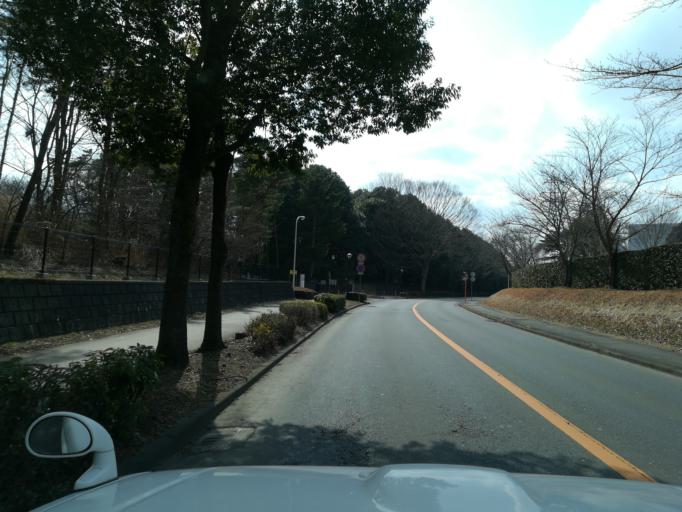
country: JP
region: Ibaraki
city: Naka
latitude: 36.0652
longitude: 140.1298
